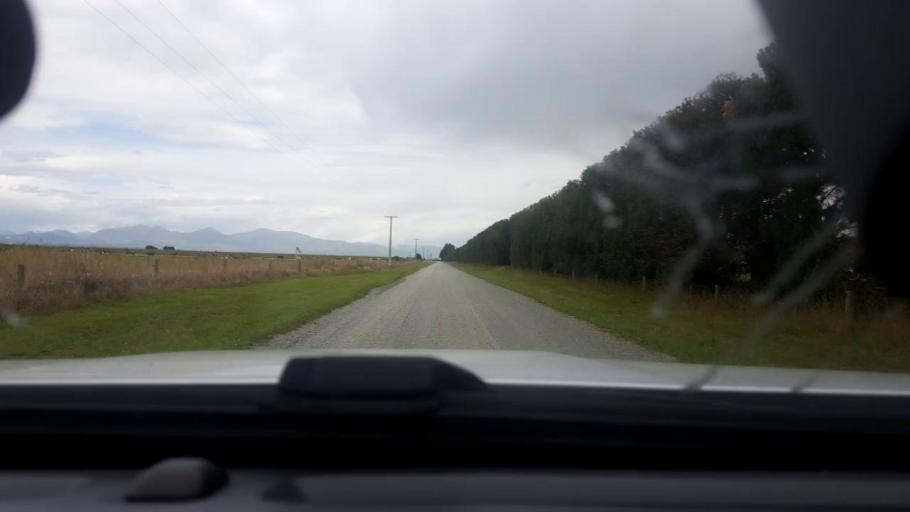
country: NZ
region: Canterbury
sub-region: Timaru District
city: Pleasant Point
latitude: -44.1488
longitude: 171.3923
